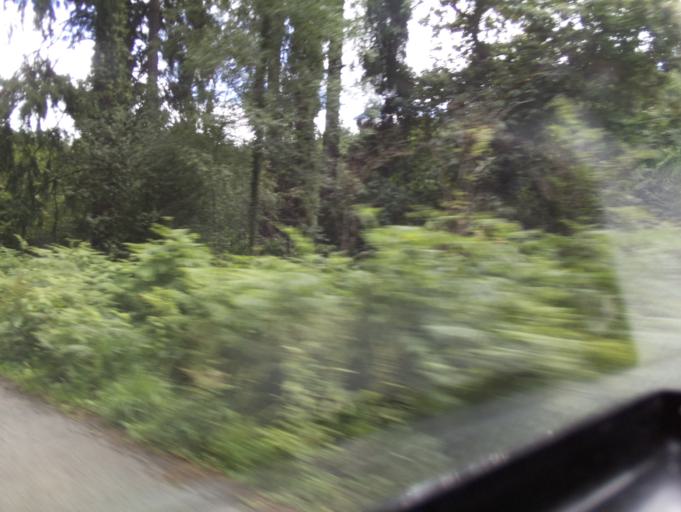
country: GB
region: England
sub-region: Gloucestershire
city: Cinderford
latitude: 51.8011
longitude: -2.4919
